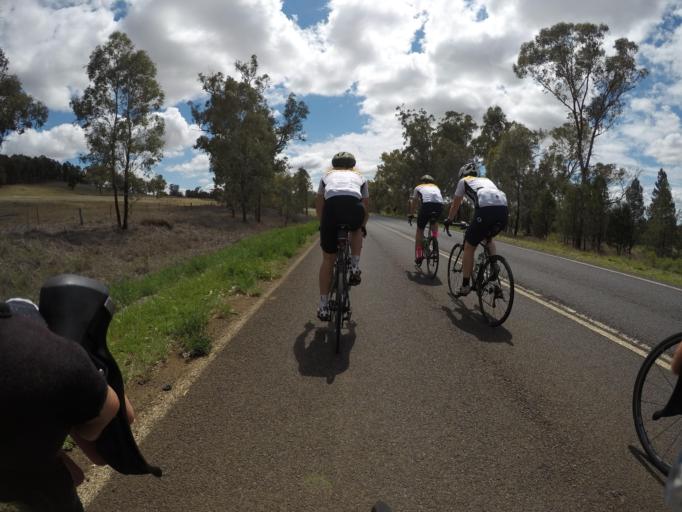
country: AU
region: New South Wales
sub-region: Dubbo Municipality
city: Dubbo
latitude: -32.4410
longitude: 148.5845
